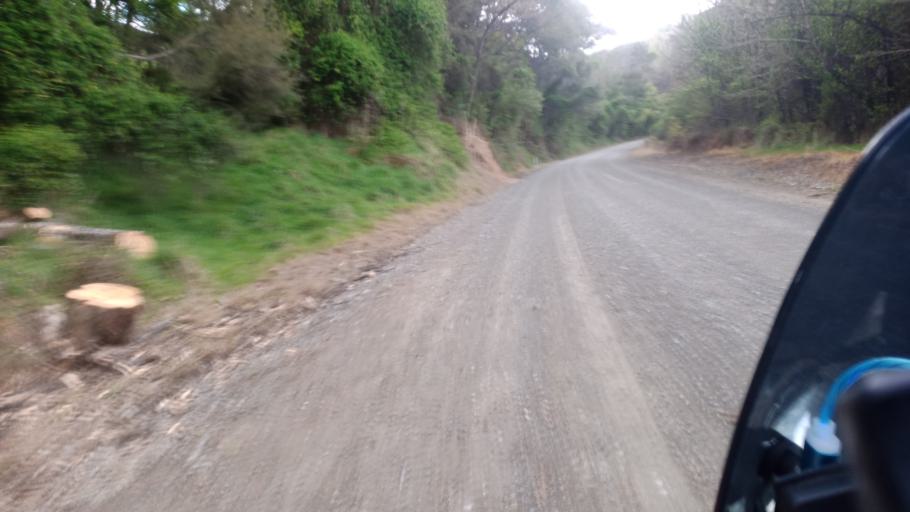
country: NZ
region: Gisborne
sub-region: Gisborne District
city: Gisborne
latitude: -38.2048
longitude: 178.2488
